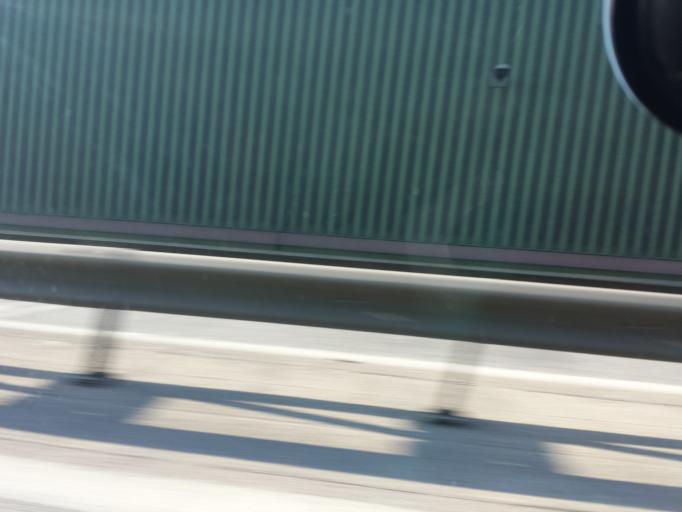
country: DE
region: Berlin
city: Tegel
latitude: 52.5852
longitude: 13.2923
